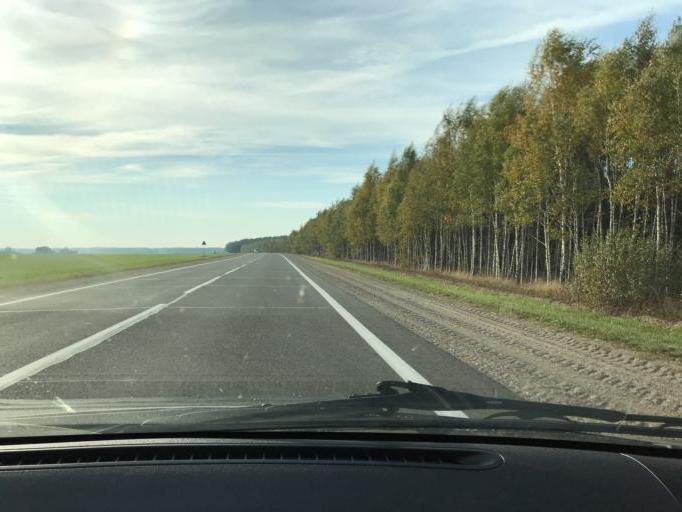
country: BY
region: Brest
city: Horad Pinsk
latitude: 52.1645
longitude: 25.9812
